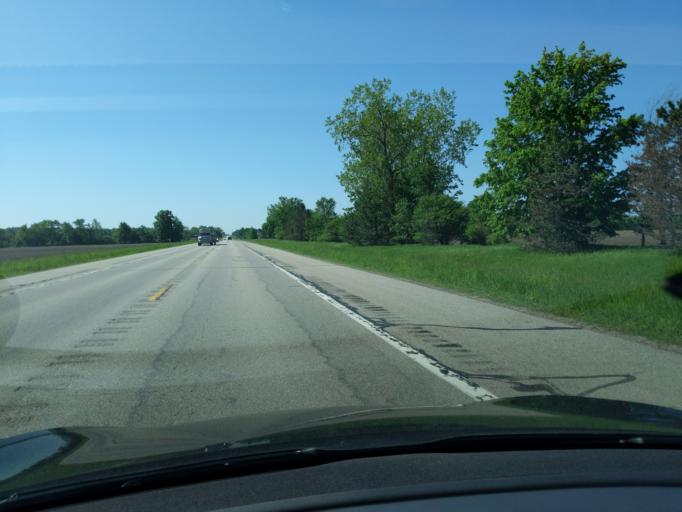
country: US
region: Michigan
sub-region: Ingham County
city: Webberville
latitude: 42.5899
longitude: -84.1933
